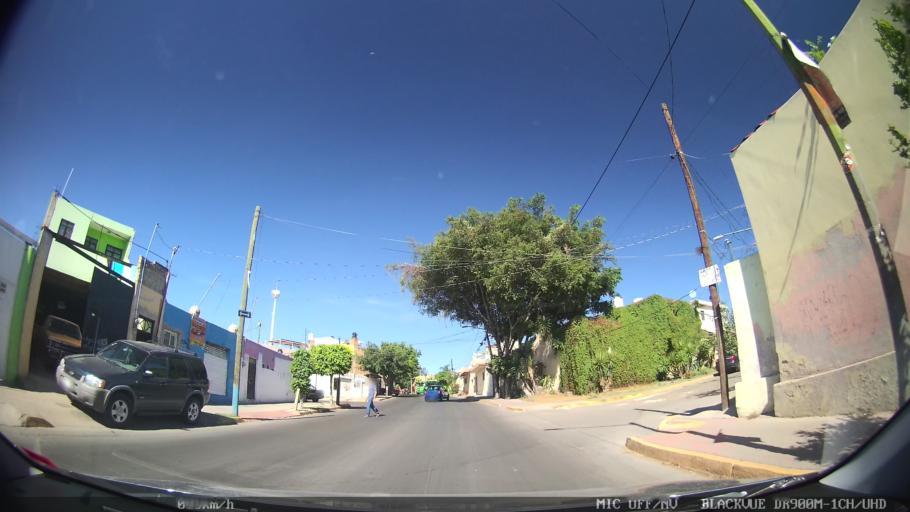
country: MX
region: Jalisco
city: Tlaquepaque
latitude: 20.6798
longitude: -103.2691
